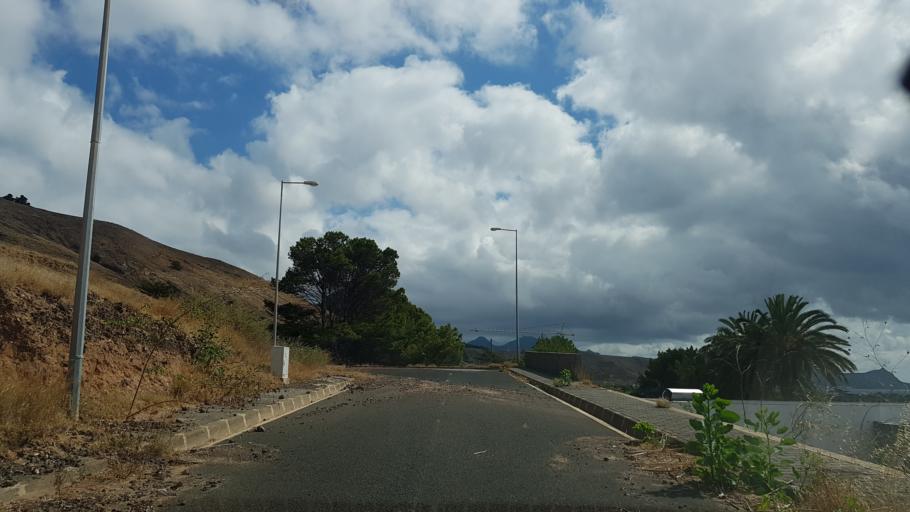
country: PT
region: Madeira
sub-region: Porto Santo
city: Vila de Porto Santo
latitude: 33.0289
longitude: -16.3783
